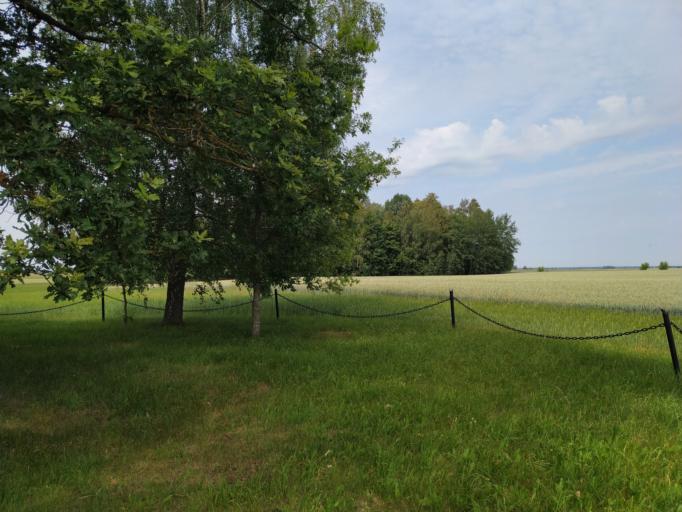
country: LT
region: Panevezys
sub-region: Birzai
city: Birzai
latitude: 56.3193
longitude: 24.6967
